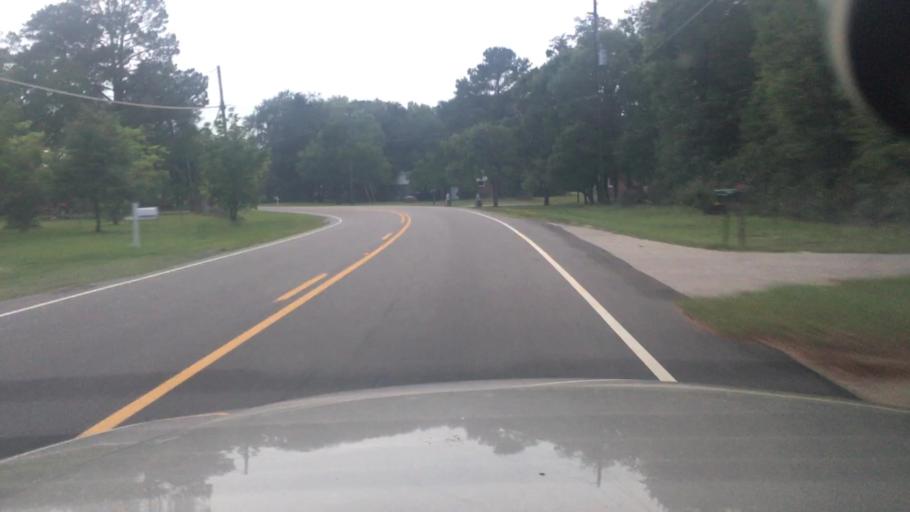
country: US
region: North Carolina
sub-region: Cumberland County
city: Hope Mills
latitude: 34.9668
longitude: -78.9255
